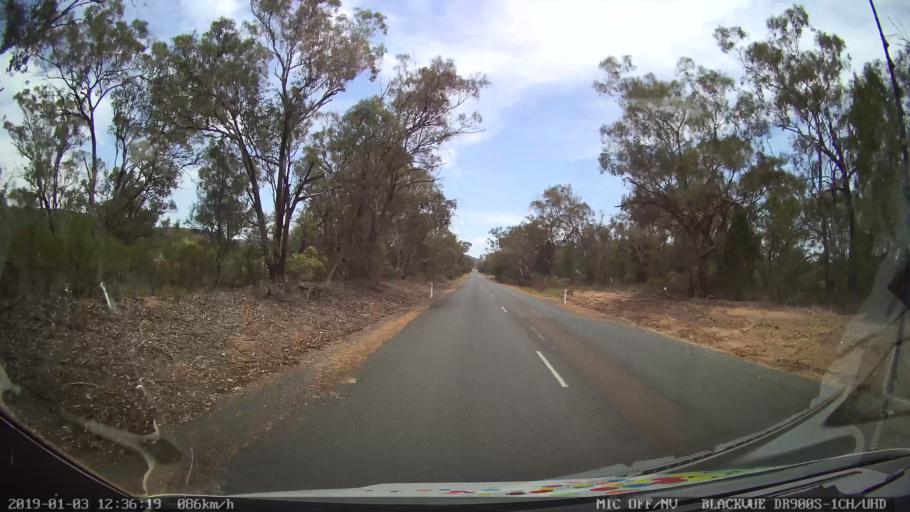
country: AU
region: New South Wales
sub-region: Weddin
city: Grenfell
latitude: -33.8564
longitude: 148.1763
